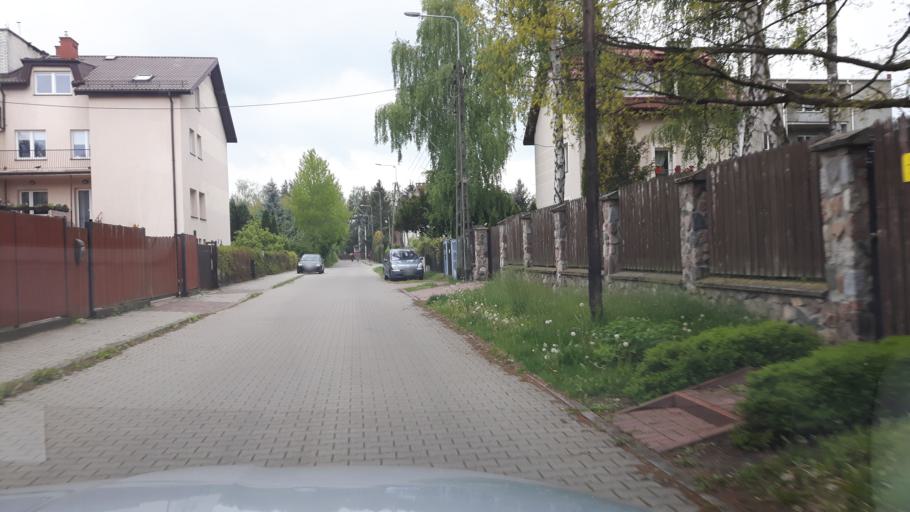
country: PL
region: Masovian Voivodeship
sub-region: Warszawa
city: Rembertow
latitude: 52.2597
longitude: 21.1814
